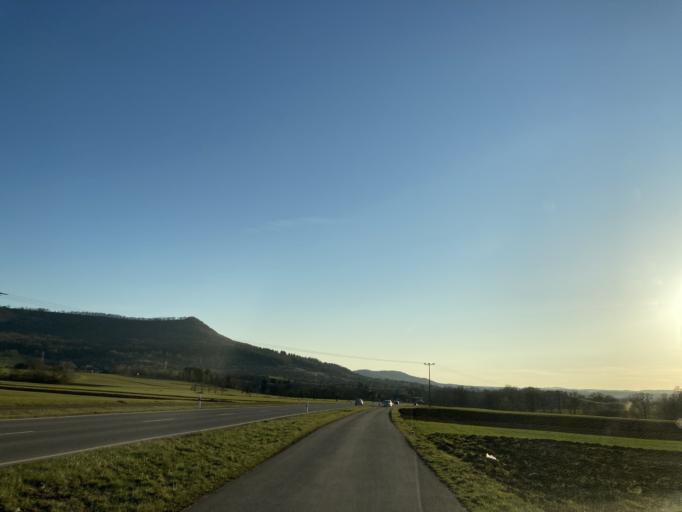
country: DE
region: Baden-Wuerttemberg
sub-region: Tuebingen Region
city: Nehren
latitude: 48.4104
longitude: 9.0938
